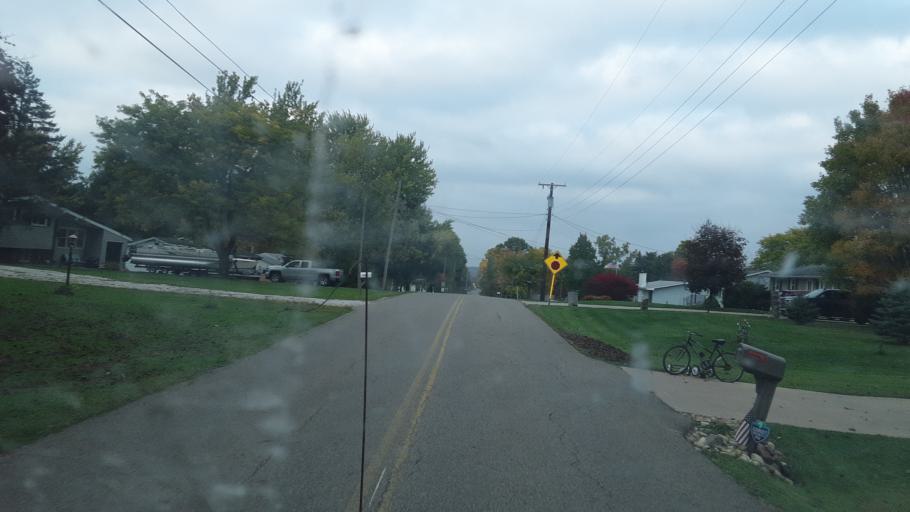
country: US
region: Ohio
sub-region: Richland County
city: Lincoln Heights
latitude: 40.7843
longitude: -82.4470
